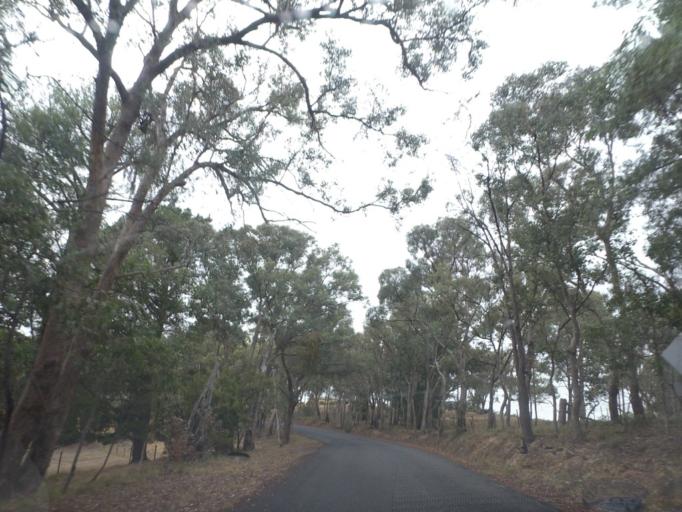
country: AU
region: Victoria
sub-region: Nillumbik
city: Saint Andrews
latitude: -37.6273
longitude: 145.2712
